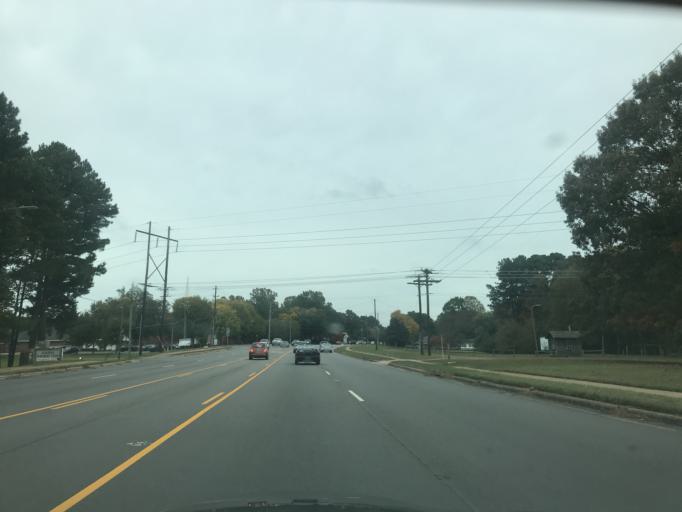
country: US
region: North Carolina
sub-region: Wake County
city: West Raleigh
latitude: 35.8586
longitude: -78.6170
